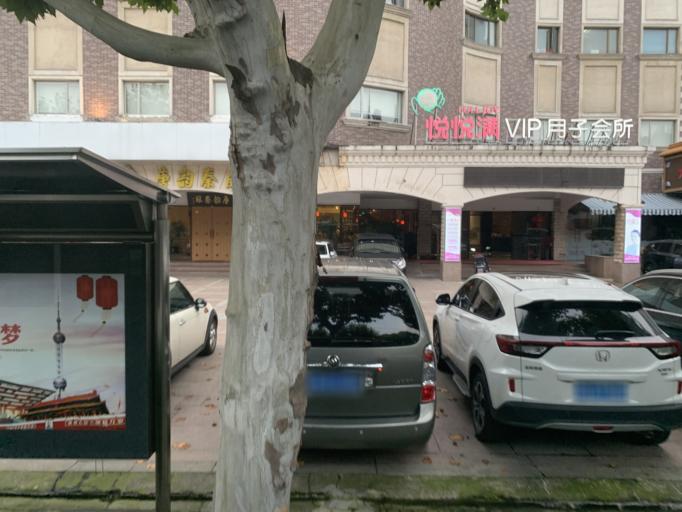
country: CN
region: Shanghai Shi
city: Pudong
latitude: 31.2392
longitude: 121.5220
